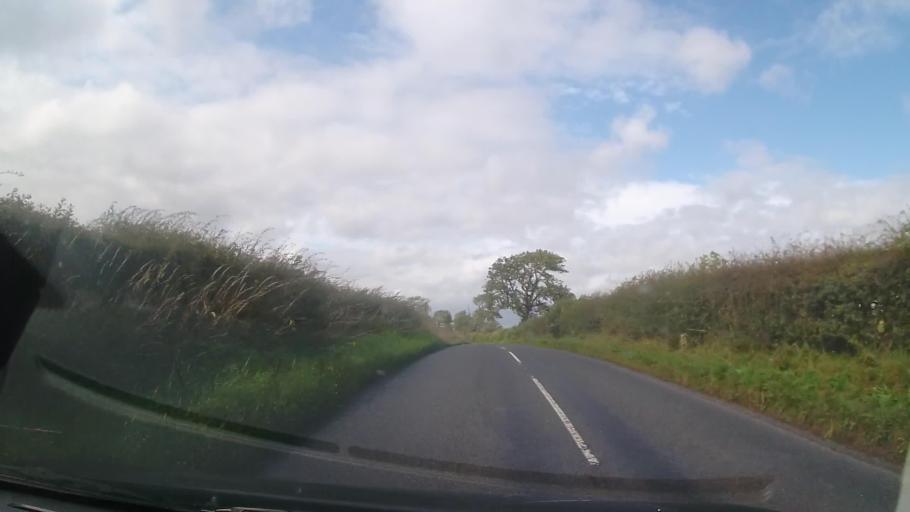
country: GB
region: Wales
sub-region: Sir Powys
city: Knighton
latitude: 52.4008
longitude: -3.0455
